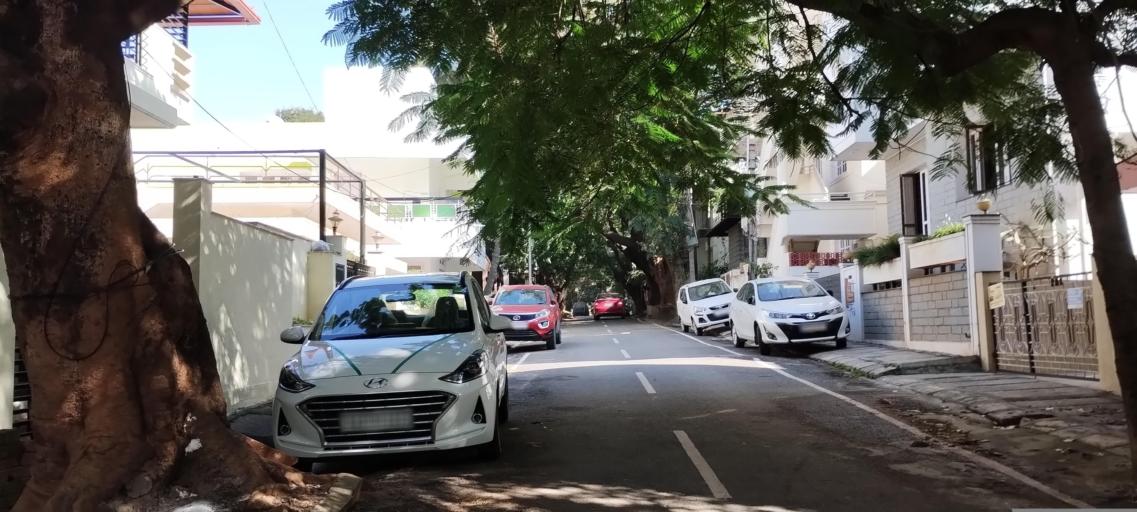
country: IN
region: Karnataka
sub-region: Bangalore Urban
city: Bangalore
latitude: 12.9349
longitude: 77.5411
